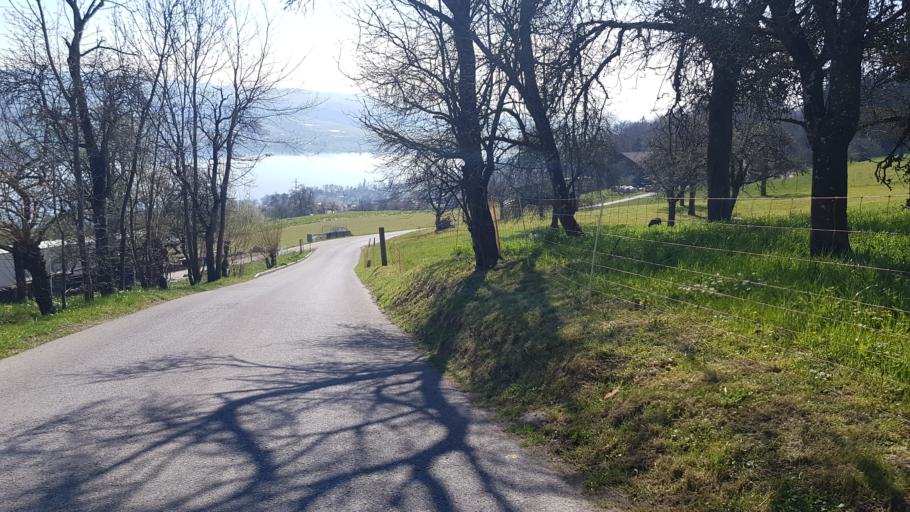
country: CH
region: Aargau
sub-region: Bezirk Kulm
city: Reinach
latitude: 47.2777
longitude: 8.1902
